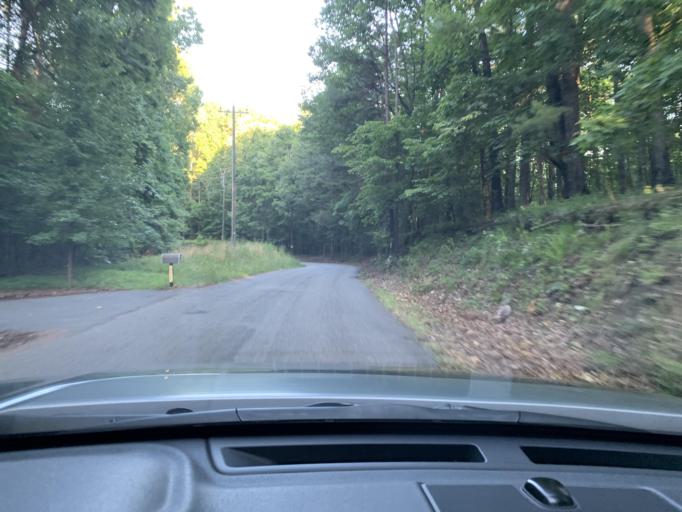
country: US
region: Georgia
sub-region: Bartow County
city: Rydal
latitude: 34.2323
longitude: -84.6443
